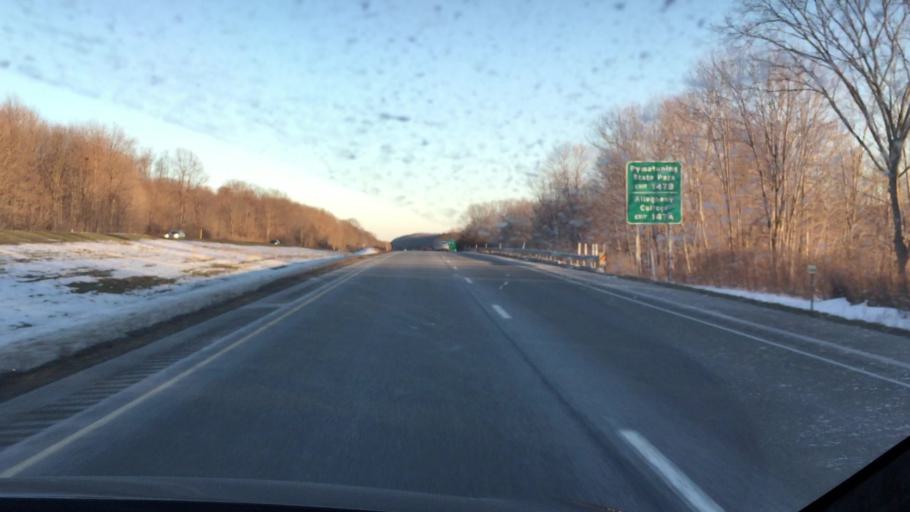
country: US
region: Pennsylvania
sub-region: Crawford County
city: Meadville
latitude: 41.6393
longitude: -80.1993
